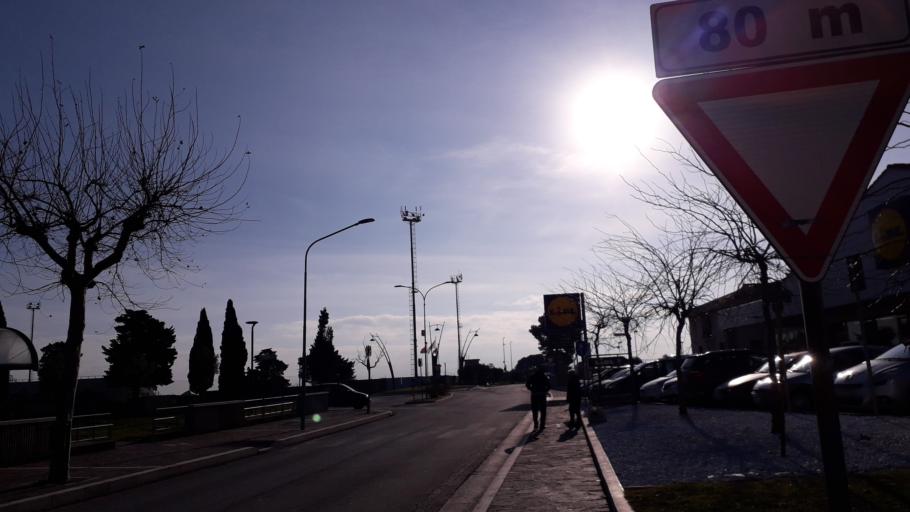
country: IT
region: Molise
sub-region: Provincia di Campobasso
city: Campomarino
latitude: 41.9522
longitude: 15.0363
